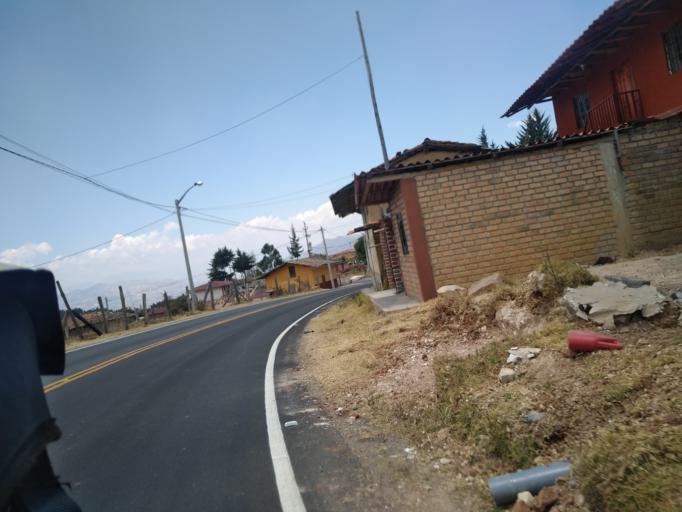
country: PE
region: Cajamarca
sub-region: San Marcos
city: San Marcos
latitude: -7.2796
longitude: -78.2406
